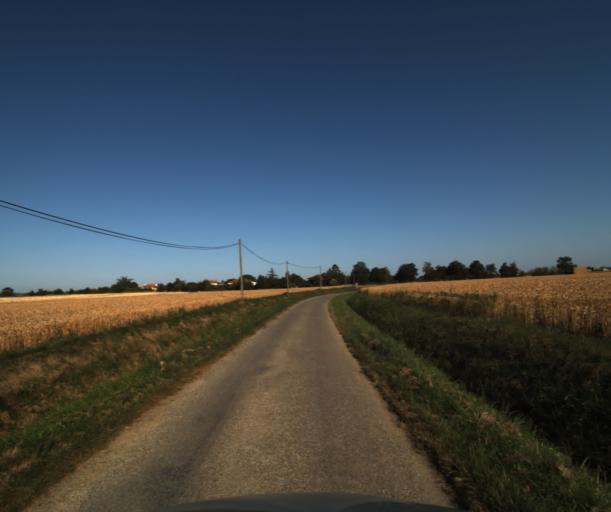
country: FR
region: Midi-Pyrenees
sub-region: Departement de la Haute-Garonne
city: Labarthe-sur-Leze
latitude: 43.4491
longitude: 1.3872
